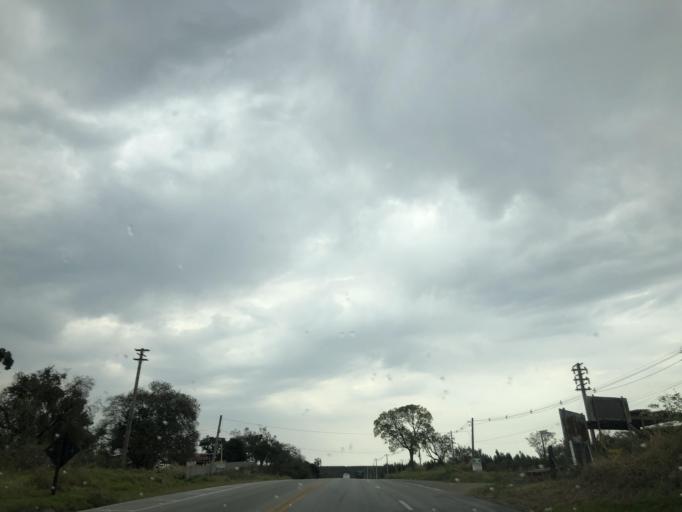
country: BR
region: Sao Paulo
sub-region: Salto De Pirapora
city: Salto de Pirapora
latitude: -23.6896
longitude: -47.6065
